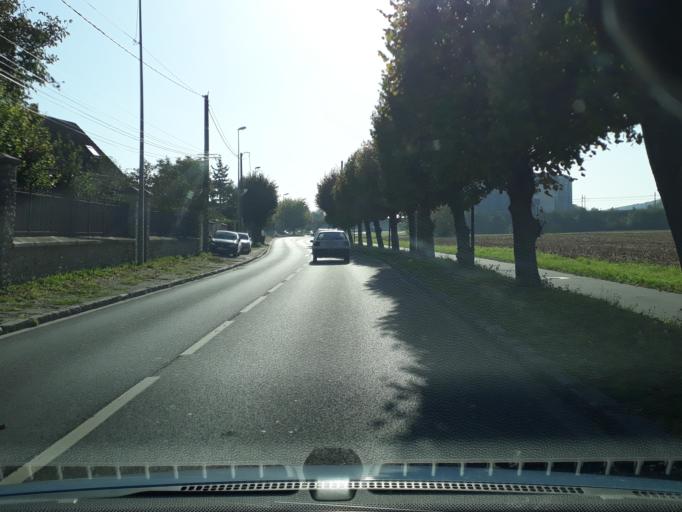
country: FR
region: Ile-de-France
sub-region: Departement de Seine-et-Marne
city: Livry-sur-Seine
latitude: 48.5223
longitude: 2.6727
